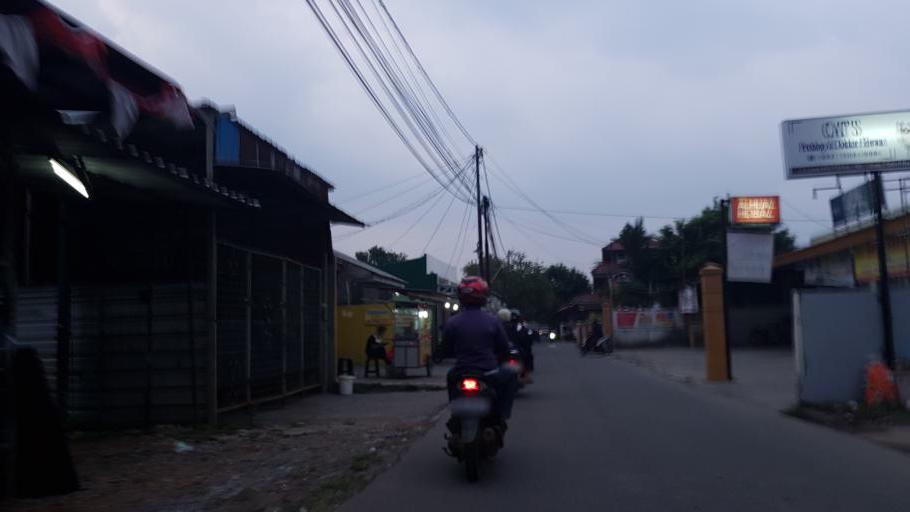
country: ID
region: West Java
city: Depok
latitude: -6.3670
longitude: 106.7981
